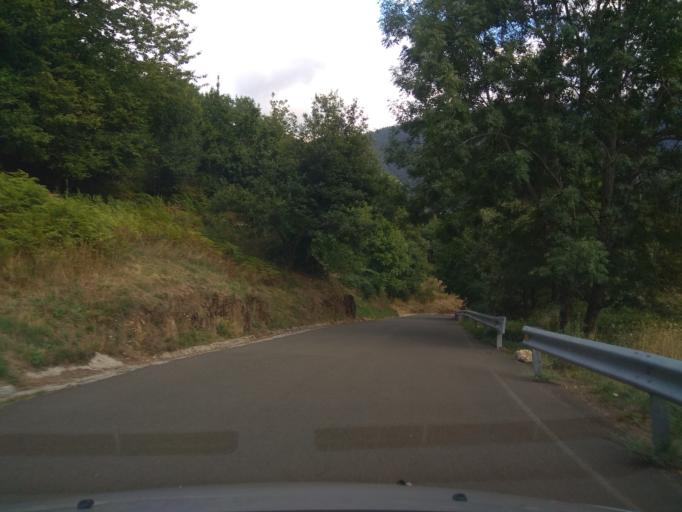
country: ES
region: Catalonia
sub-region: Provincia de Lleida
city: Les
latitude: 42.8341
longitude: 0.7197
